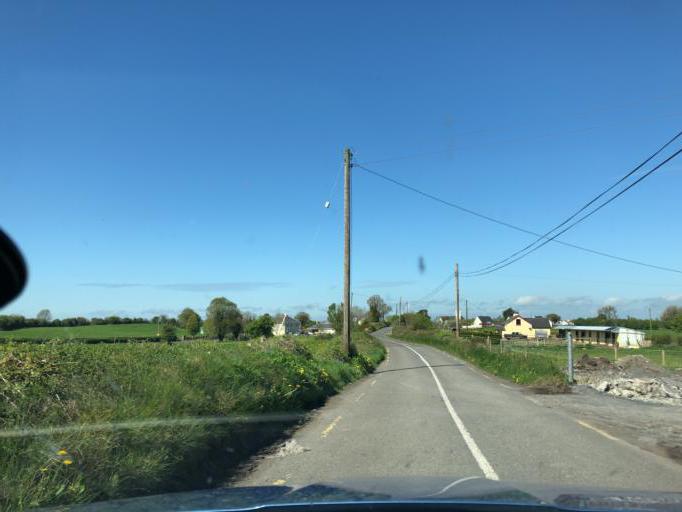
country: IE
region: Connaught
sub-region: County Galway
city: Portumna
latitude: 53.1625
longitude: -8.2762
